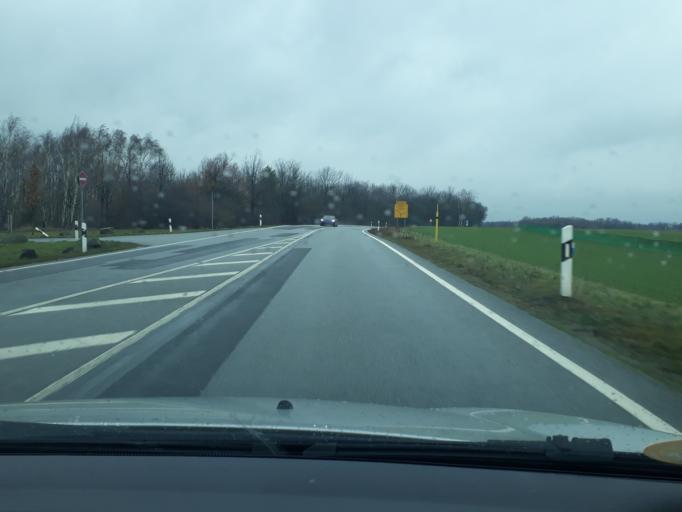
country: DE
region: Saxony
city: Grossdubrau
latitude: 51.2088
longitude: 14.4719
